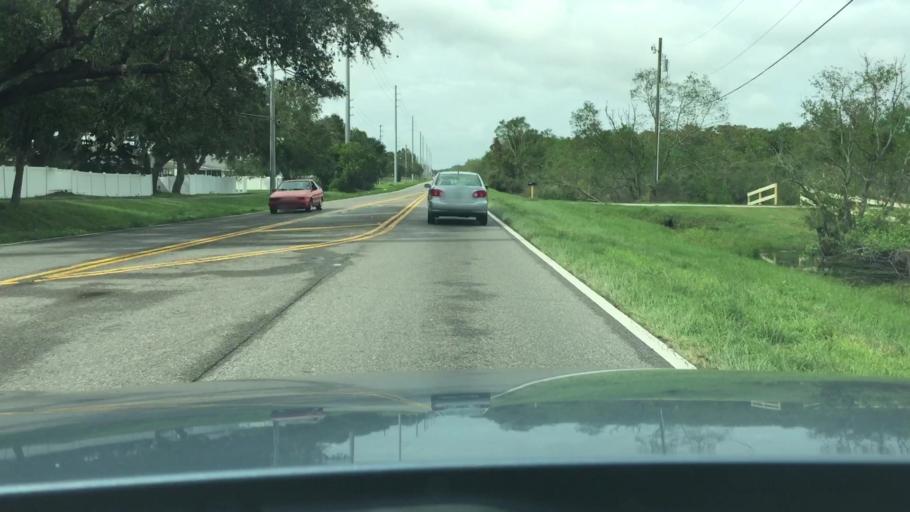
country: US
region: Florida
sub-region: Osceola County
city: Buenaventura Lakes
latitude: 28.2686
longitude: -81.3509
